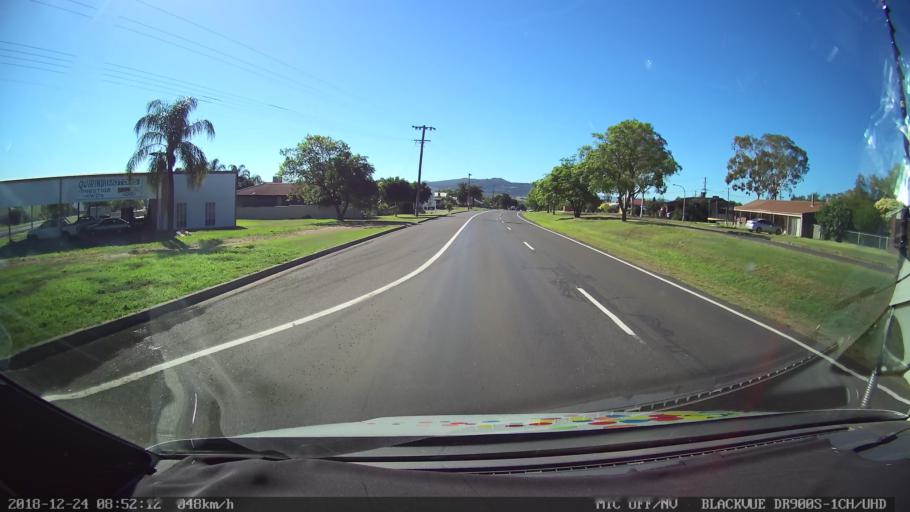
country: AU
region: New South Wales
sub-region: Liverpool Plains
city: Quirindi
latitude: -31.4900
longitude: 150.6781
